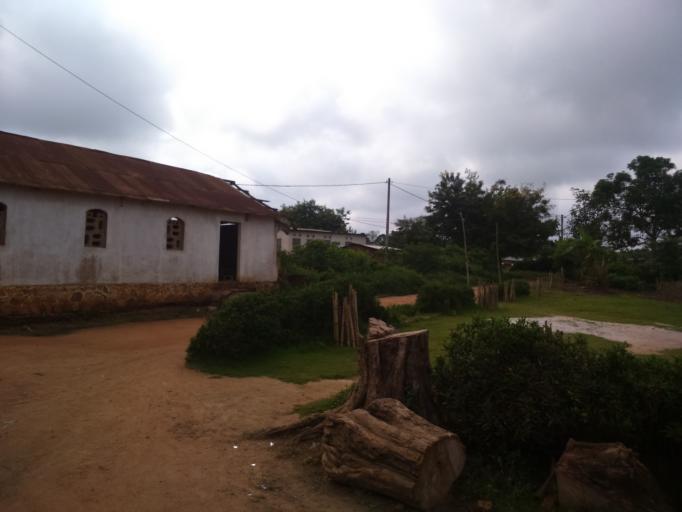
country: CI
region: Agneby
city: Agboville
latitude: 6.0271
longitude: -4.1317
